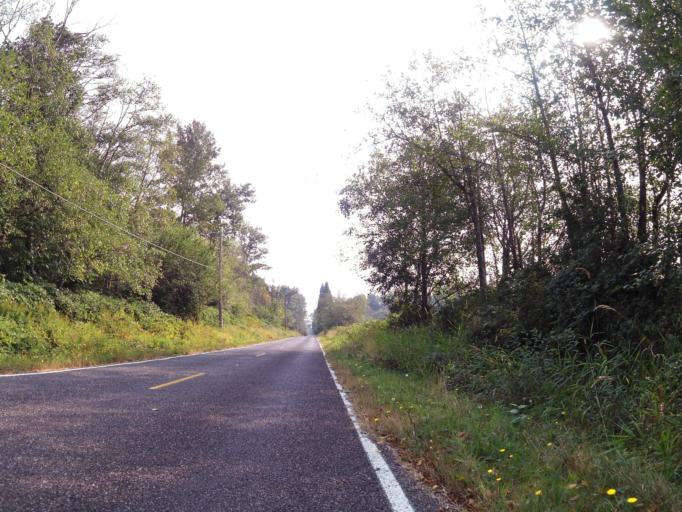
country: US
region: Washington
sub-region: Whatcom County
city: Birch Bay
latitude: 48.8631
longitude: -122.7202
